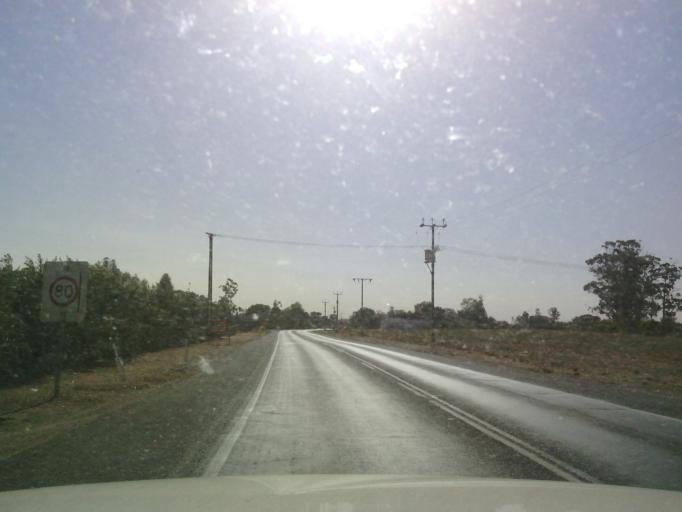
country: AU
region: South Australia
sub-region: Berri and Barmera
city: Berri
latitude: -34.2820
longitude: 140.5890
